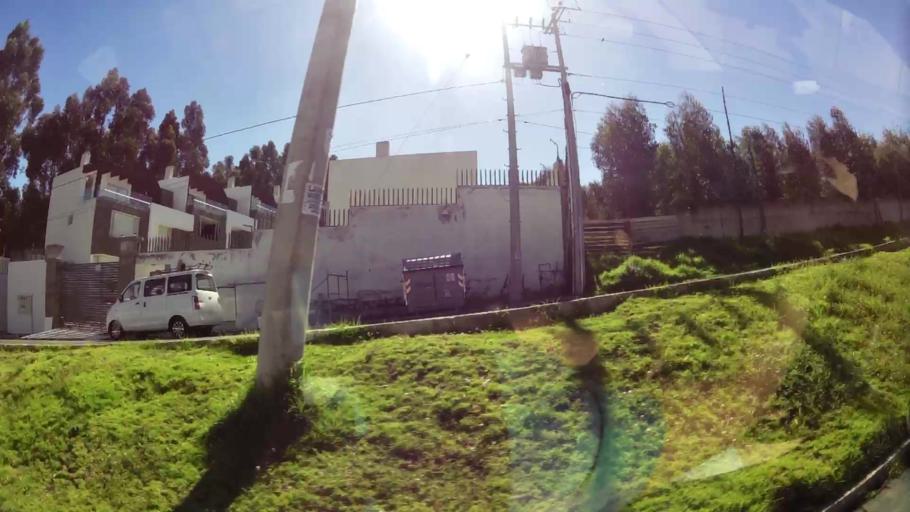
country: EC
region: Pichincha
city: Quito
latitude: -0.1234
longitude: -78.4774
